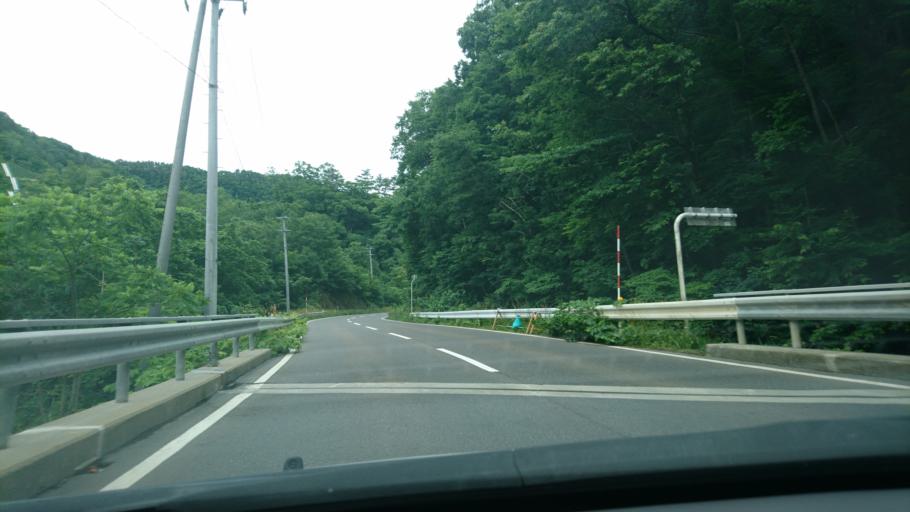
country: JP
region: Iwate
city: Miyako
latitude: 39.9833
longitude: 141.8639
